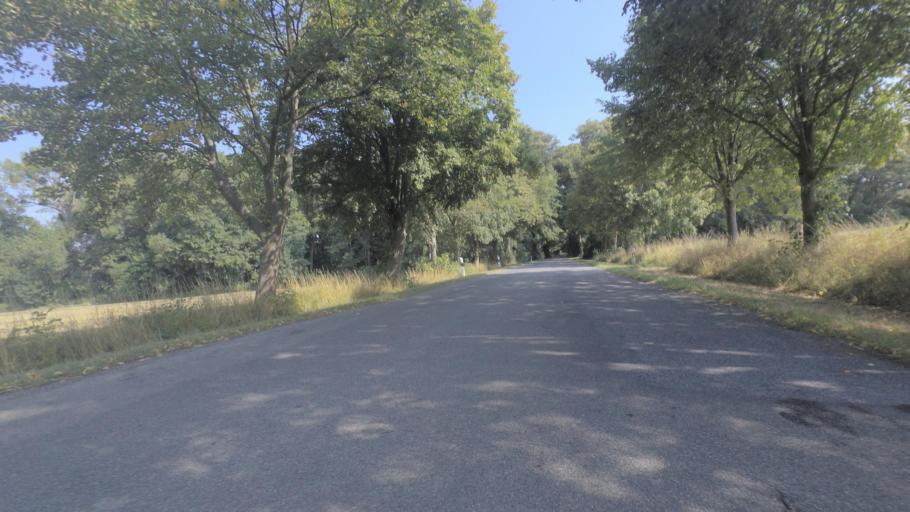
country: DE
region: Mecklenburg-Vorpommern
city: Pampow
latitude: 53.6767
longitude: 12.5542
